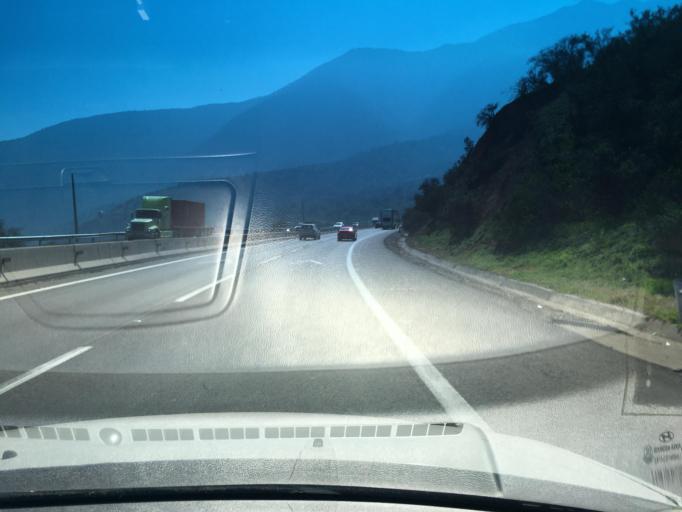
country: CL
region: Santiago Metropolitan
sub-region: Provincia de Talagante
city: Penaflor
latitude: -33.4476
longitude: -70.9814
